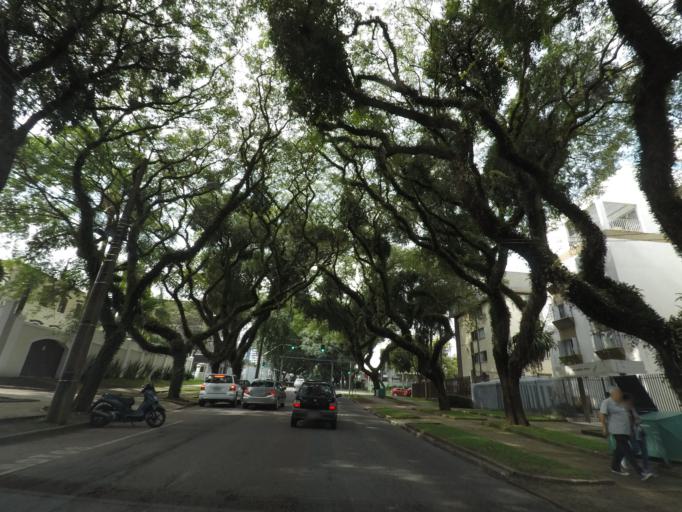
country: BR
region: Parana
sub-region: Curitiba
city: Curitiba
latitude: -25.4534
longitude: -49.2940
